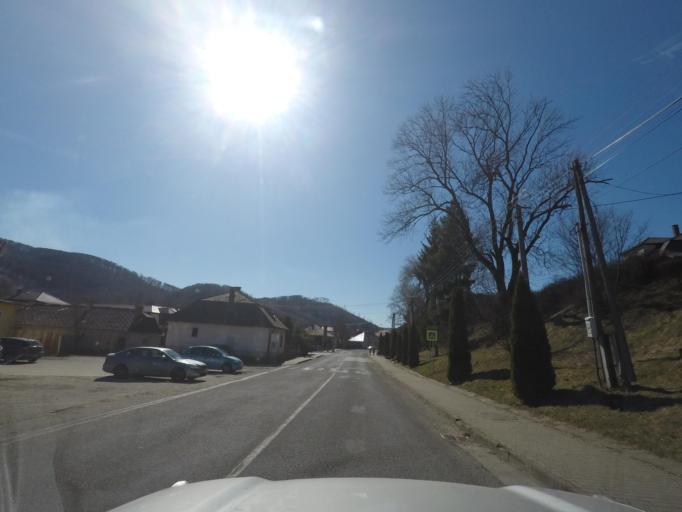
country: UA
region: Zakarpattia
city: Velykyi Bereznyi
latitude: 48.8994
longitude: 22.3917
